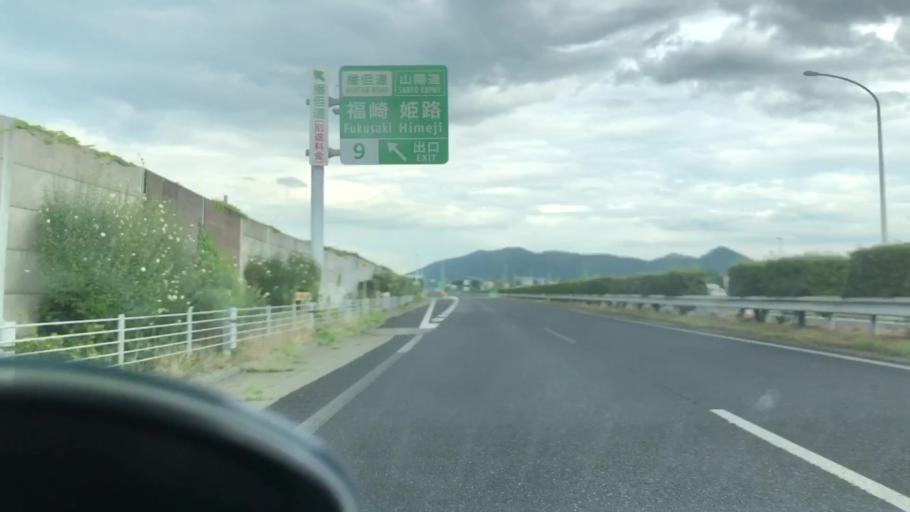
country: JP
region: Hyogo
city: Himeji
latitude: 34.9493
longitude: 134.7600
